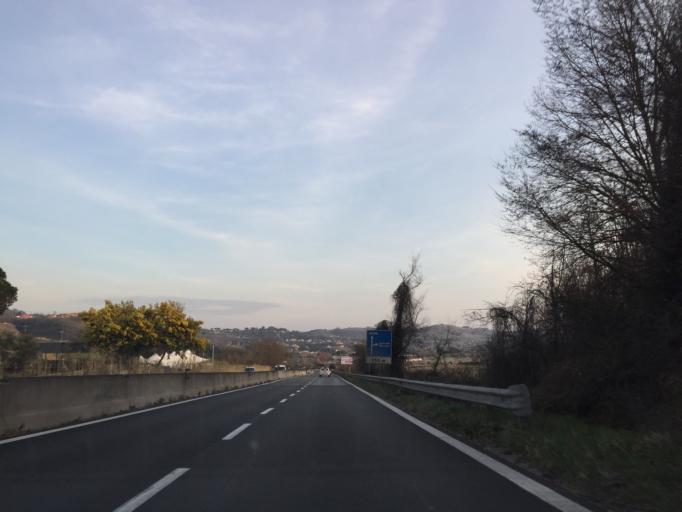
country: IT
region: Latium
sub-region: Citta metropolitana di Roma Capitale
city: Campagnano di Roma
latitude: 42.1330
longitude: 12.3552
